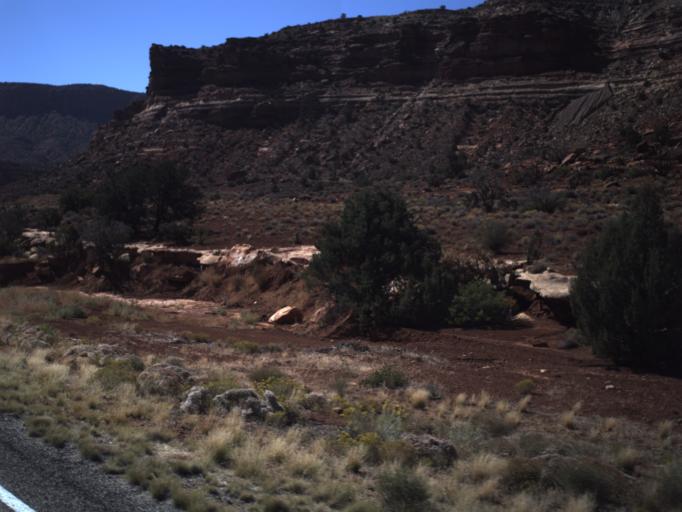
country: US
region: Utah
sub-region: San Juan County
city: Blanding
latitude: 37.7533
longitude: -110.2805
